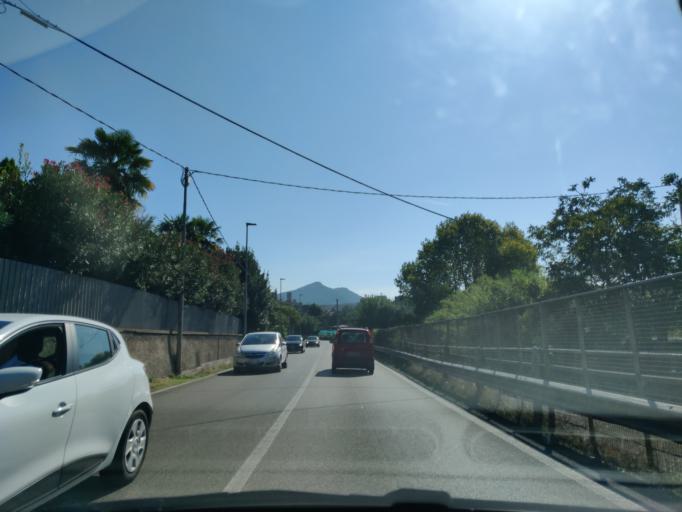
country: IT
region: Latium
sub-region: Provincia di Viterbo
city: Viterbo
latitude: 42.4152
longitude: 12.0942
